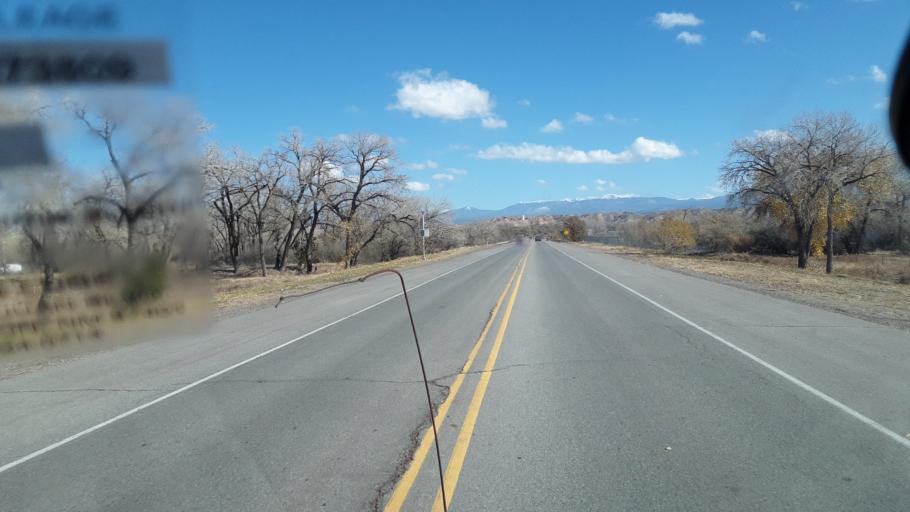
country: US
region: New Mexico
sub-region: Rio Arriba County
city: Espanola
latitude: 36.0082
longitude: -106.0760
